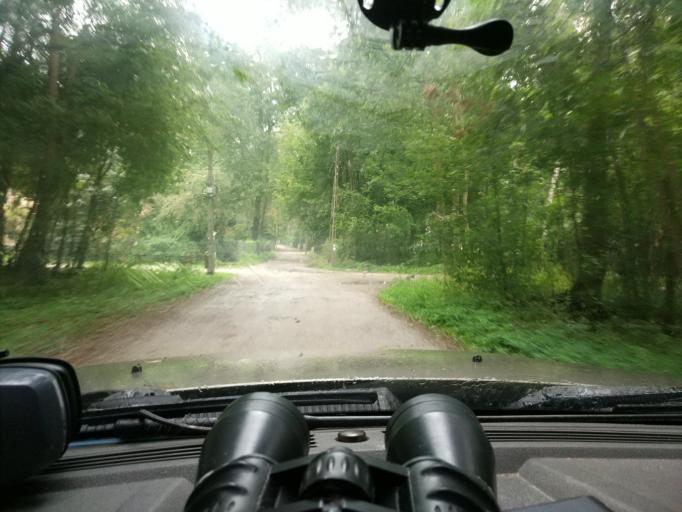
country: PL
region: Masovian Voivodeship
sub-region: Powiat grodziski
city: Podkowa Lesna
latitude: 52.1262
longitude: 20.7357
